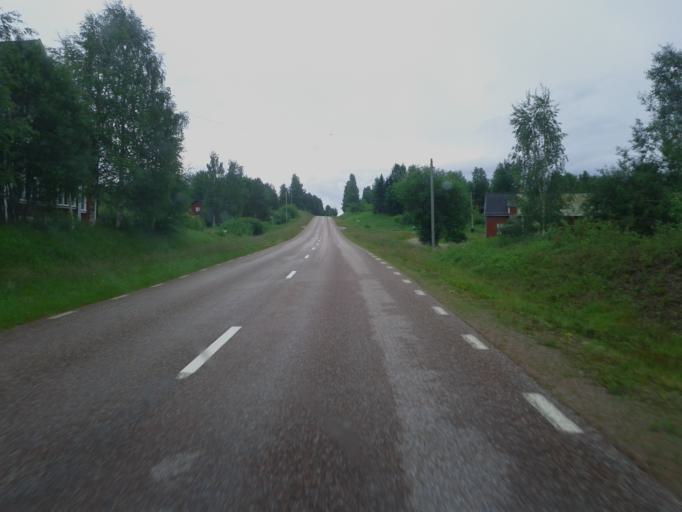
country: NO
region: Hedmark
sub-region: Trysil
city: Innbygda
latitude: 61.7347
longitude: 12.9823
